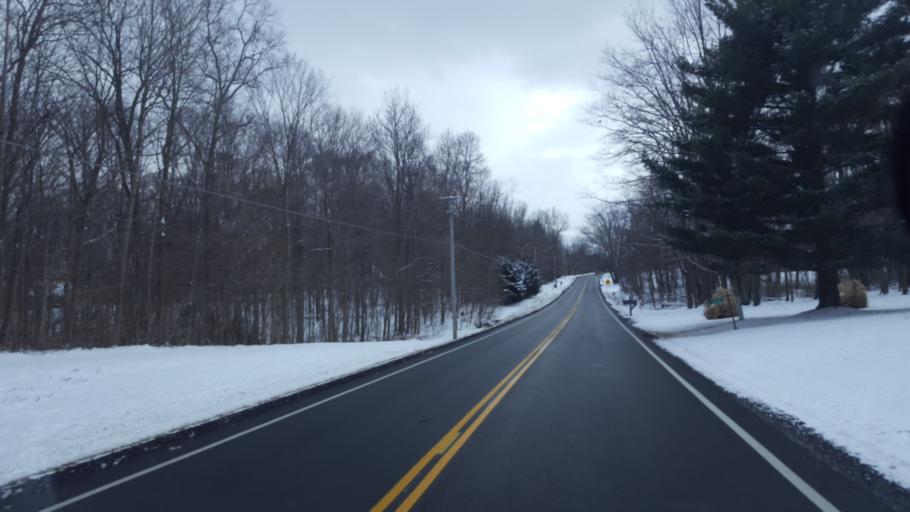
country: US
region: Ohio
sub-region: Richland County
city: Ontario
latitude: 40.7294
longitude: -82.6657
